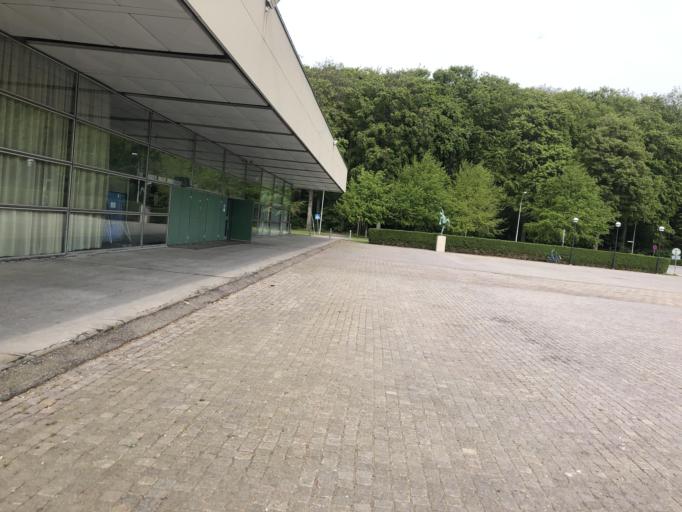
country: SE
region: Skane
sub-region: Landskrona
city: Landskrona
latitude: 55.8891
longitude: 12.8364
